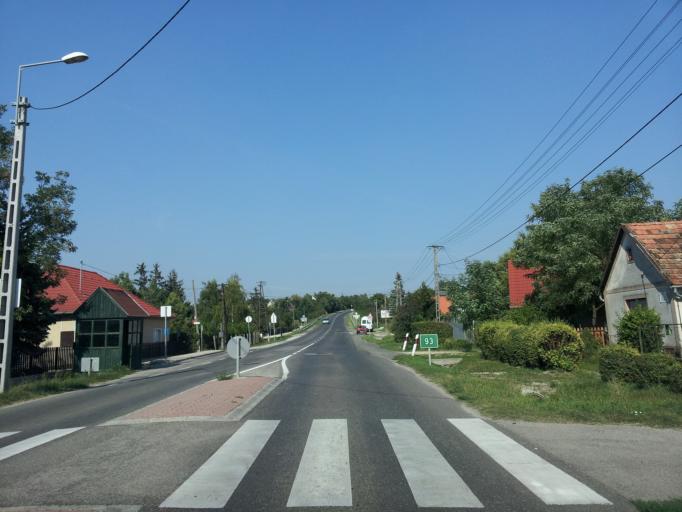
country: HU
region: Fejer
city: Lepseny
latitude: 47.0016
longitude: 18.2541
